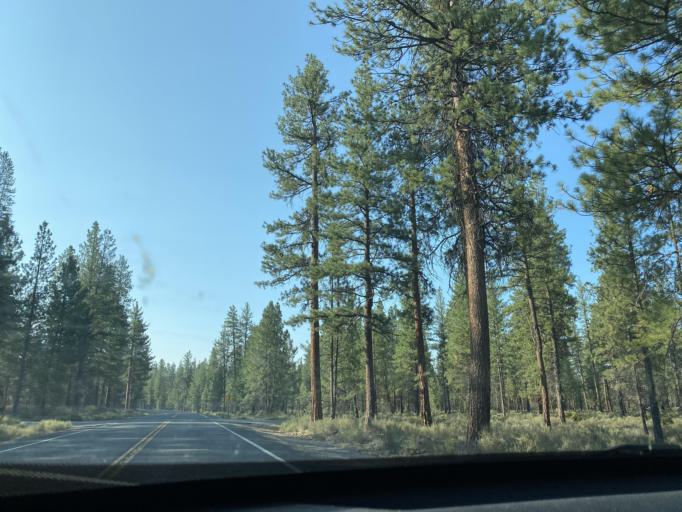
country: US
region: Oregon
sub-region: Deschutes County
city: La Pine
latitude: 43.7145
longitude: -121.4123
